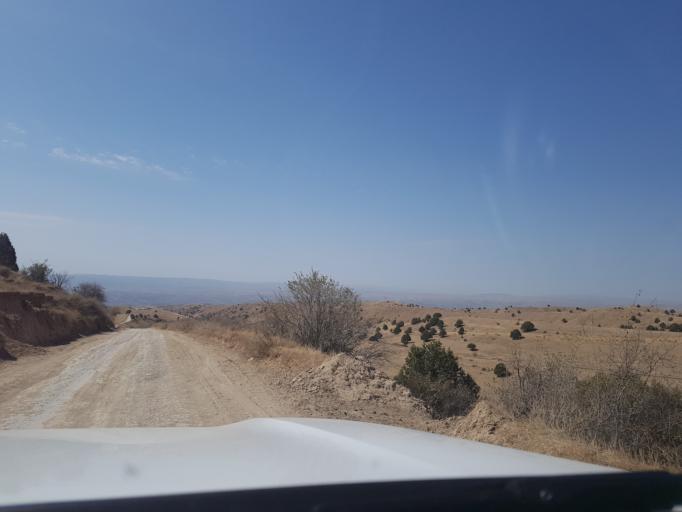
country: TM
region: Ahal
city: Baharly
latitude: 38.3051
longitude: 56.9458
